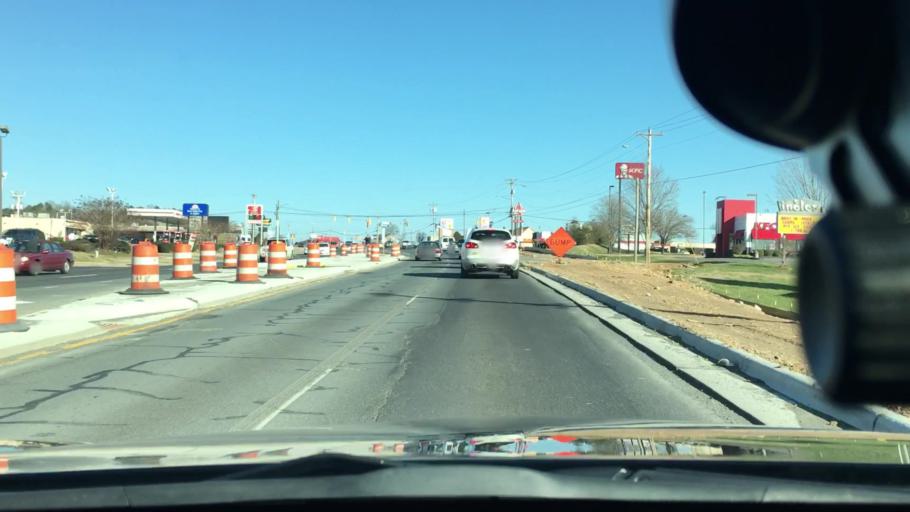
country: US
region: North Carolina
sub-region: Stanly County
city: Albemarle
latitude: 35.3439
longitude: -80.1737
